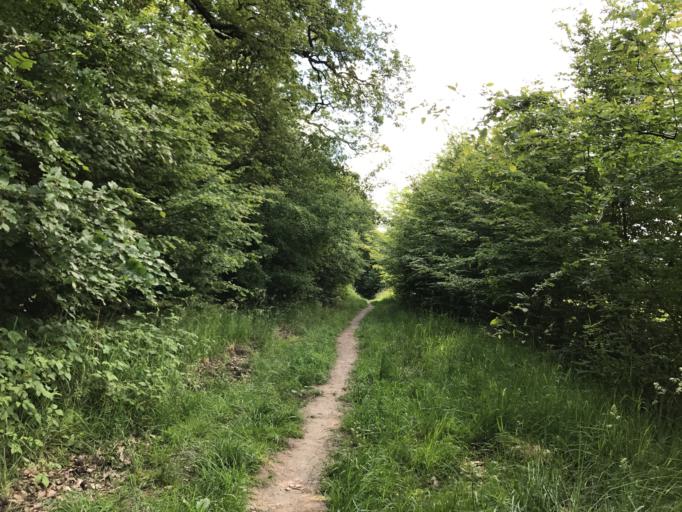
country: DE
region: Hesse
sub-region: Regierungsbezirk Darmstadt
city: Schlangenbad
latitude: 50.0832
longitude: 8.1273
